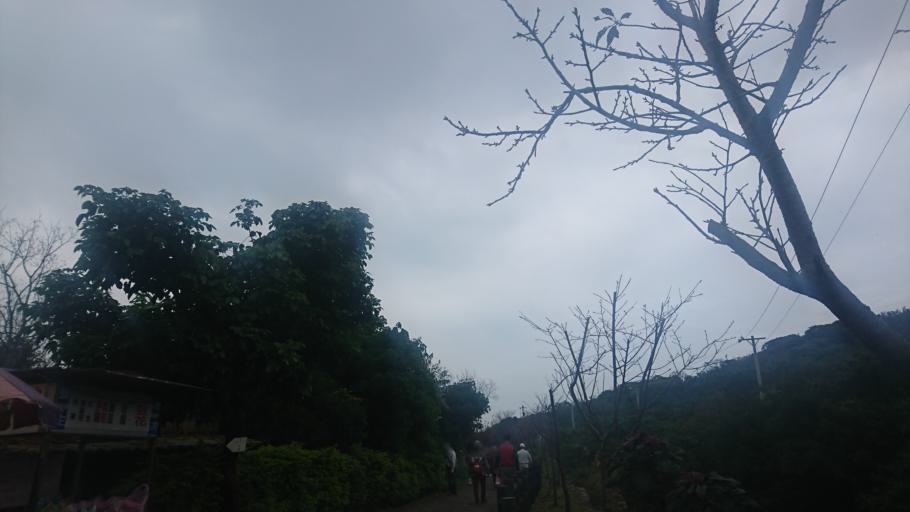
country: TW
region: Taipei
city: Taipei
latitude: 25.2648
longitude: 121.5137
